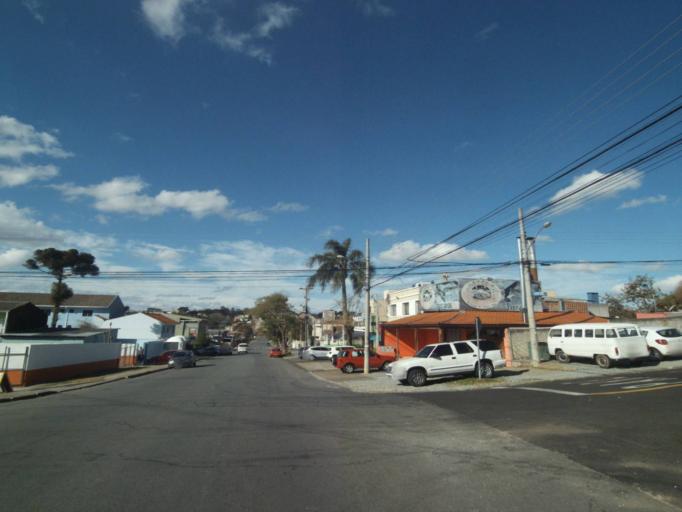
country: BR
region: Parana
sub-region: Curitiba
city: Curitiba
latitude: -25.3861
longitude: -49.2491
